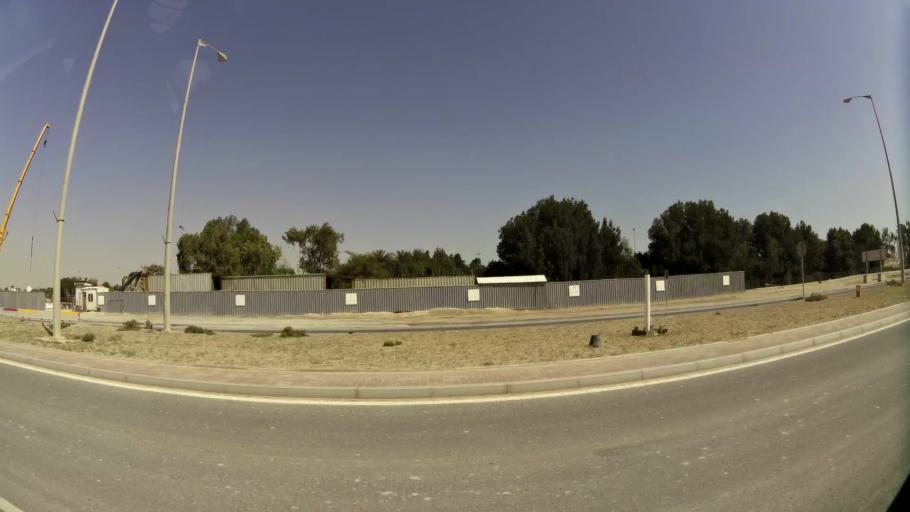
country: QA
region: Baladiyat ad Dawhah
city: Doha
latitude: 25.3773
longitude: 51.5076
